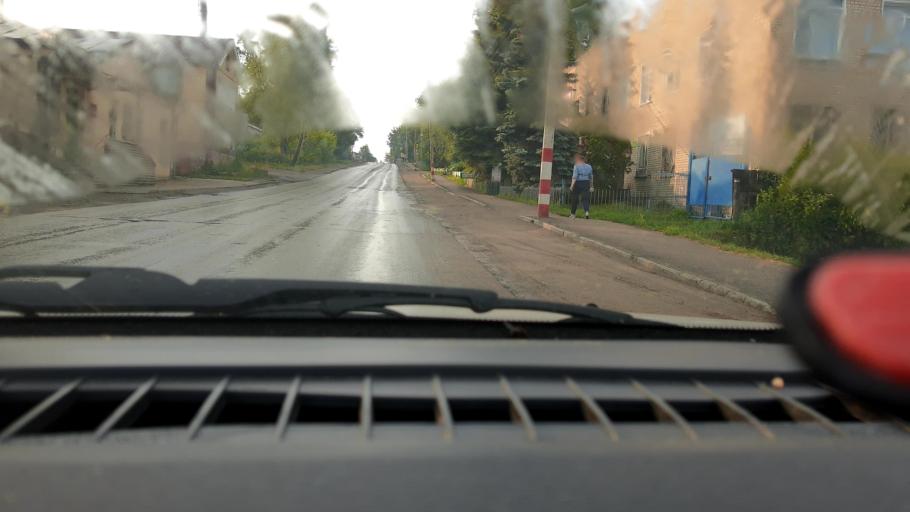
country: RU
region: Nizjnij Novgorod
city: Lukoyanov
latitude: 55.0323
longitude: 44.4950
